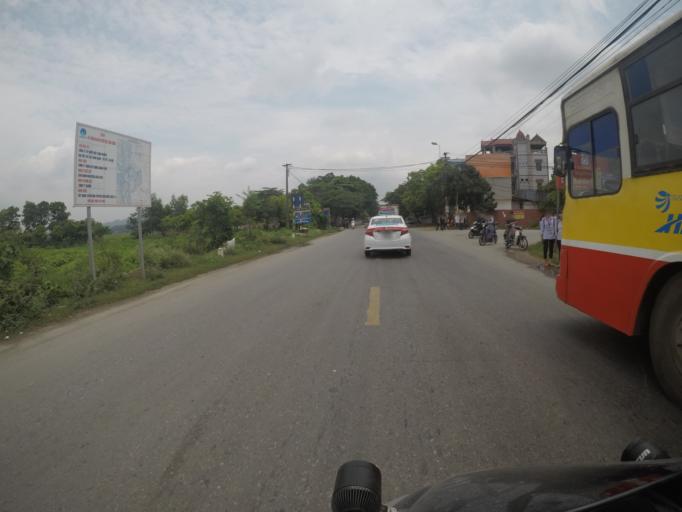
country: VN
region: Ha Noi
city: Soc Son
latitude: 21.2449
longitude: 105.8489
